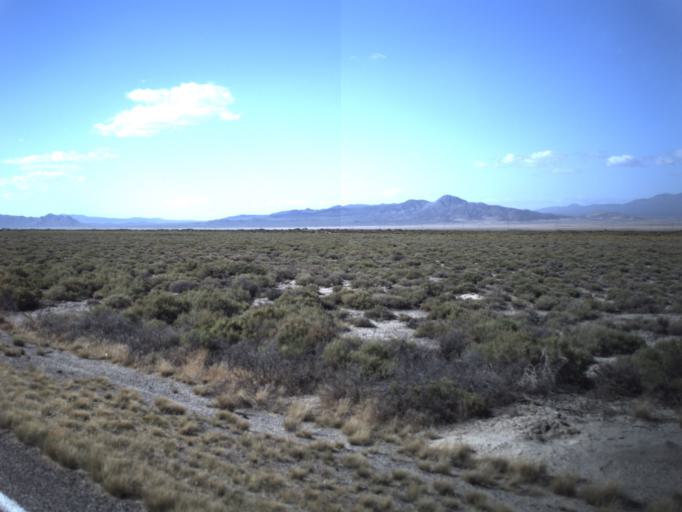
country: US
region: Utah
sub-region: Beaver County
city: Milford
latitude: 38.6316
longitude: -112.9842
